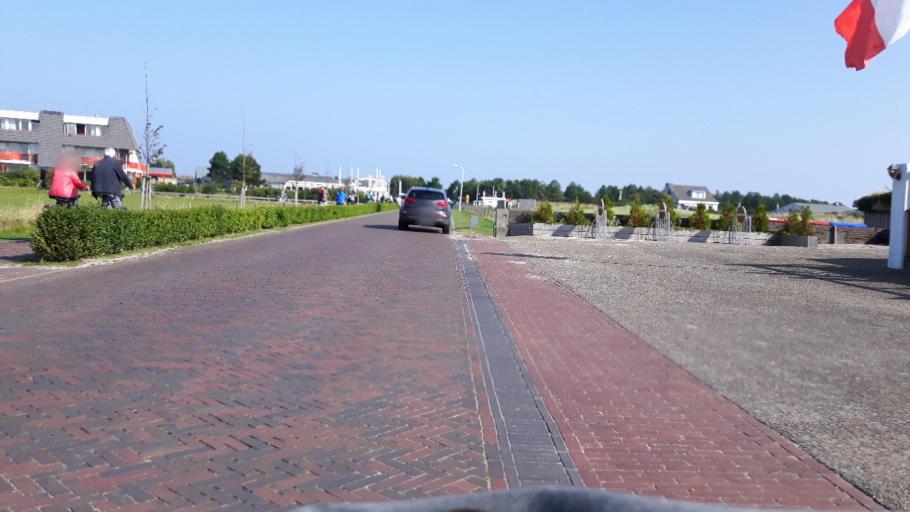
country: NL
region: Friesland
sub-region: Gemeente Ameland
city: Nes
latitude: 53.4518
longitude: 5.8017
